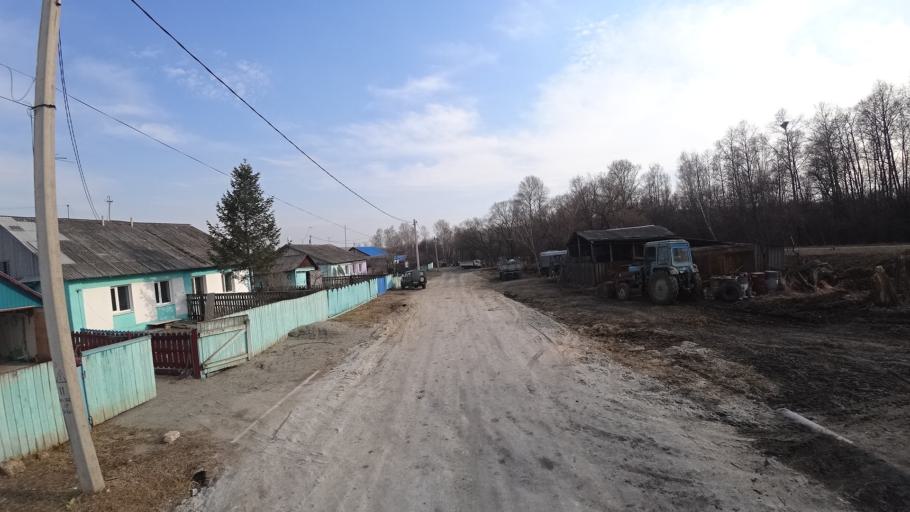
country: RU
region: Amur
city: Novobureyskiy
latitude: 49.8944
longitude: 129.8752
